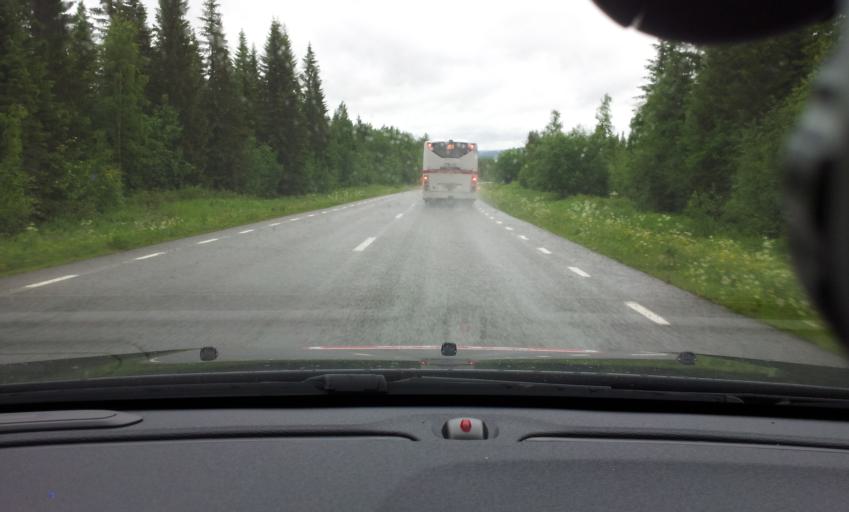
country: SE
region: Jaemtland
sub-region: Krokoms Kommun
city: Krokom
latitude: 63.5854
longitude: 14.6361
